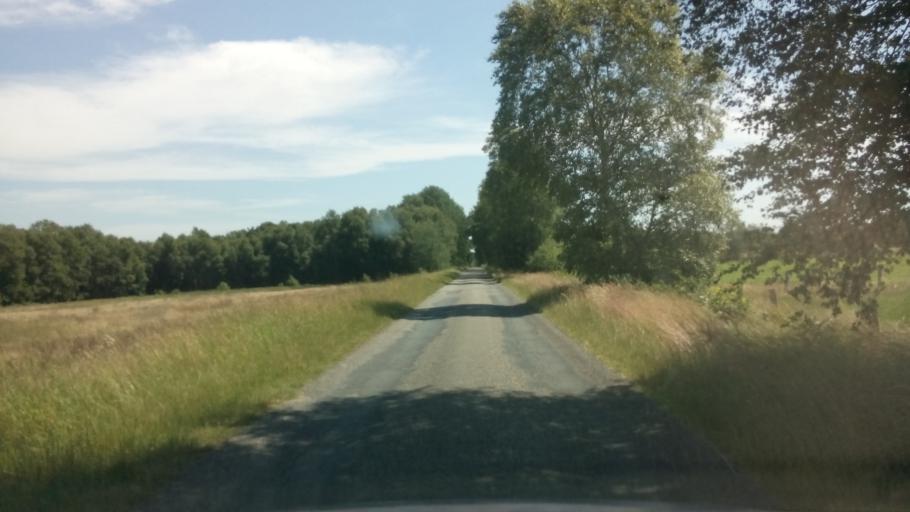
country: DE
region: Lower Saxony
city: Hambergen
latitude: 53.2661
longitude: 8.8308
